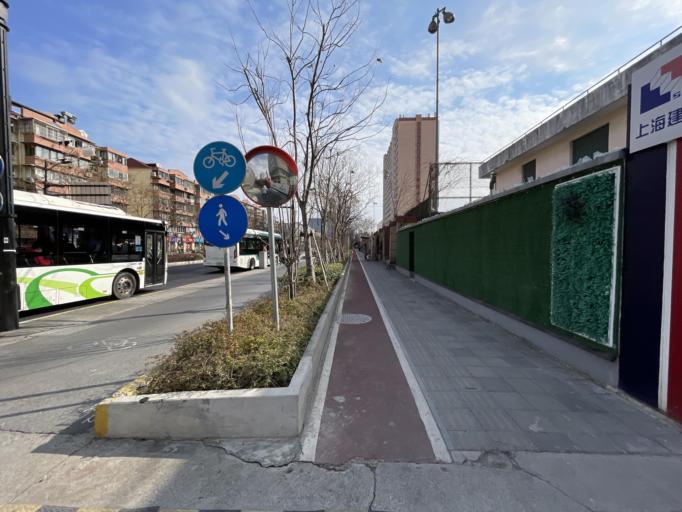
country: CN
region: Shanghai Shi
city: Yangpu
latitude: 31.3098
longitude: 121.4927
